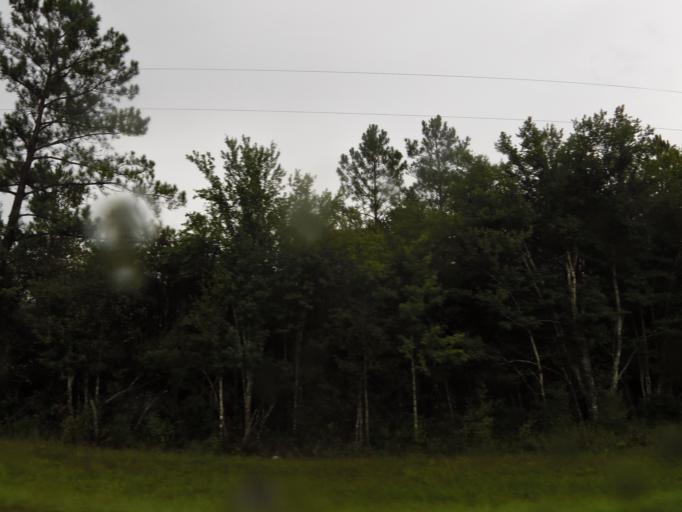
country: US
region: Georgia
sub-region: Wayne County
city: Jesup
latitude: 31.5499
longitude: -81.8736
